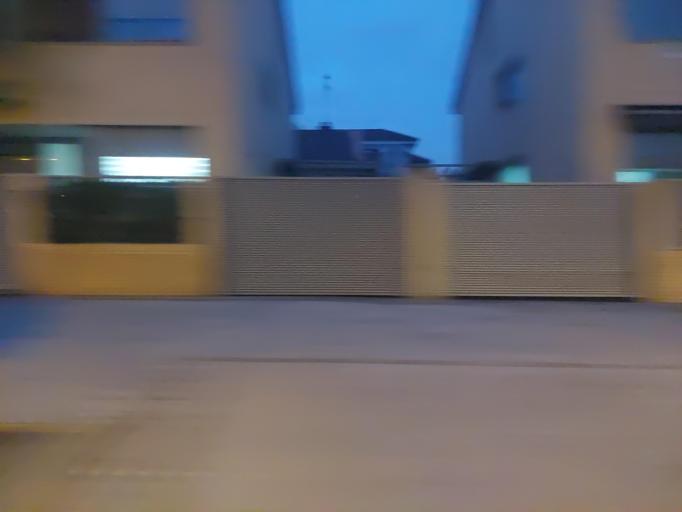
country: ES
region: Madrid
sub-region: Provincia de Madrid
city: Leganes
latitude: 40.3189
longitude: -3.7545
